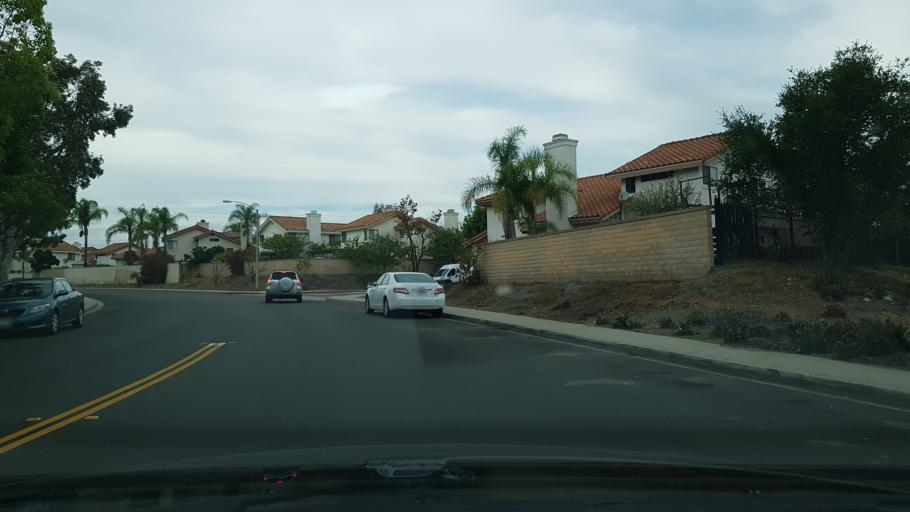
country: US
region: California
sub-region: San Diego County
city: Fairbanks Ranch
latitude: 32.9094
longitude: -117.1669
